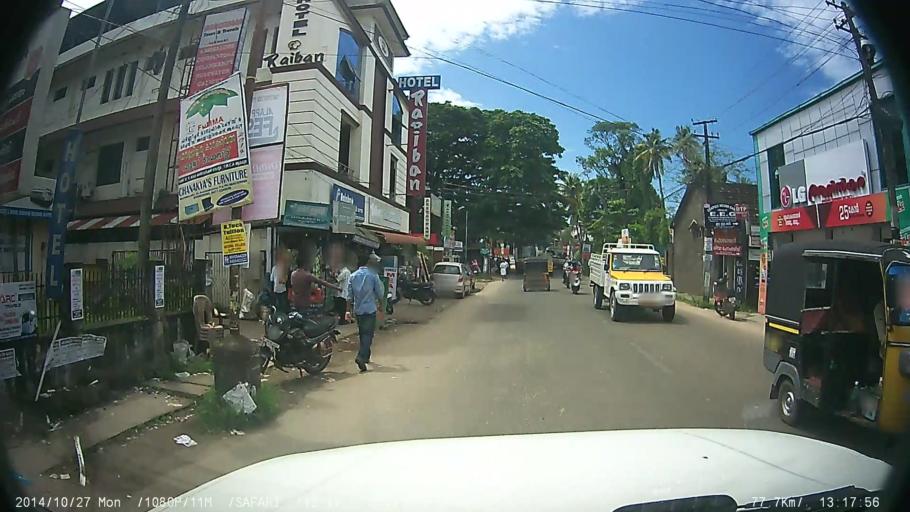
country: IN
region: Kerala
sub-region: Alappuzha
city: Alleppey
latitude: 9.4915
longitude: 76.3375
